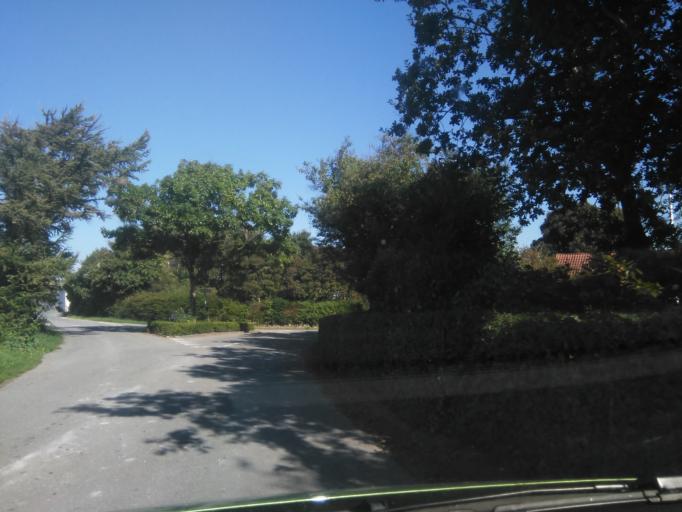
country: DK
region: Central Jutland
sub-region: Syddjurs Kommune
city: Ronde
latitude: 56.1785
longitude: 10.4222
